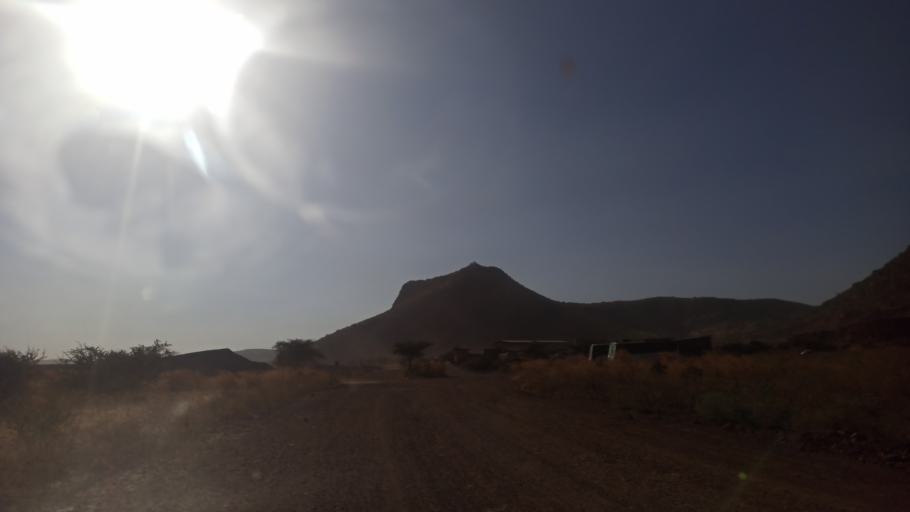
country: ET
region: Oromiya
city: Ziway
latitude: 7.9352
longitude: 38.6170
